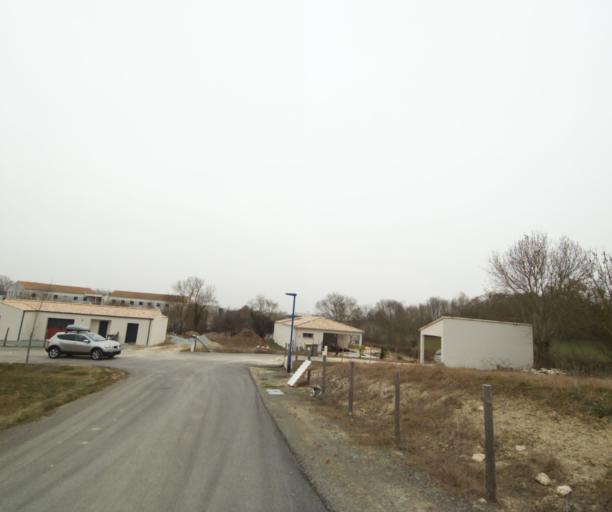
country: FR
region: Poitou-Charentes
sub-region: Departement des Deux-Sevres
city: Bessines
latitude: 46.2977
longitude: -0.4945
